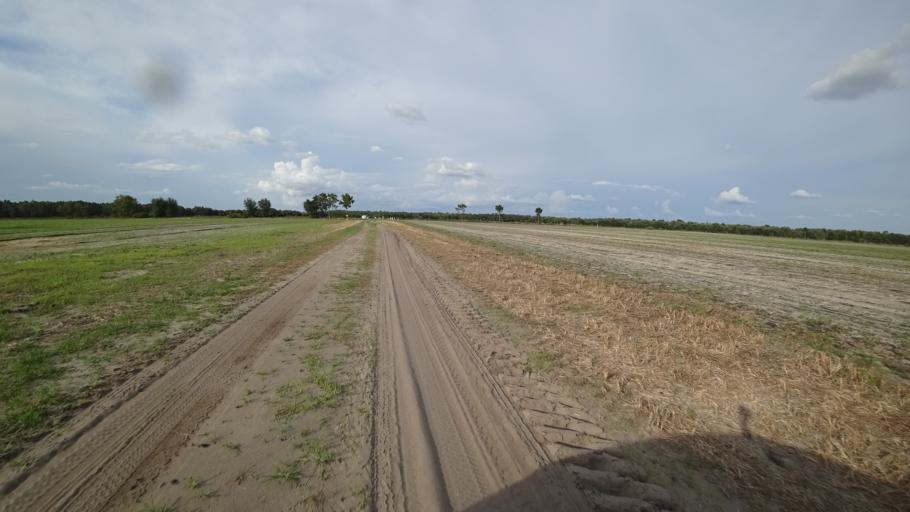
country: US
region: Florida
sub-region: Hillsborough County
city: Wimauma
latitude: 27.5579
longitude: -82.0955
